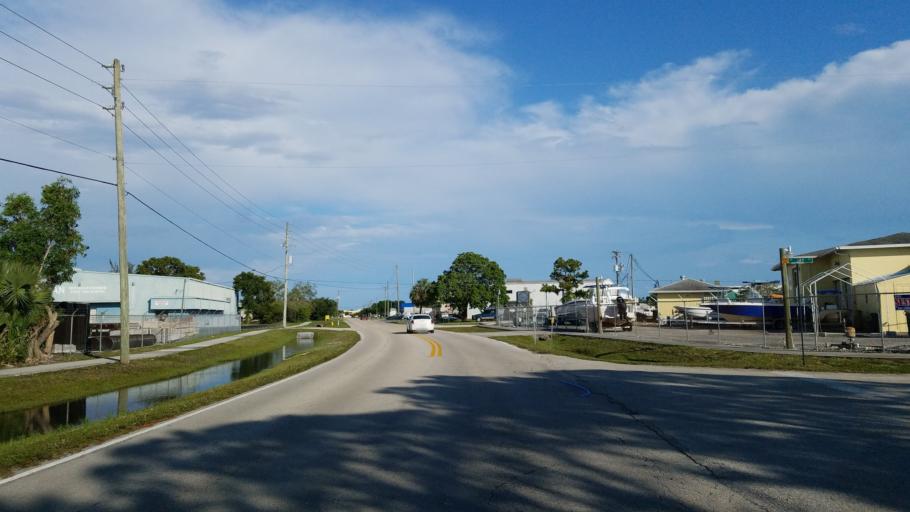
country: US
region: Florida
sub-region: Martin County
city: Port Salerno
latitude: 27.1544
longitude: -80.2110
